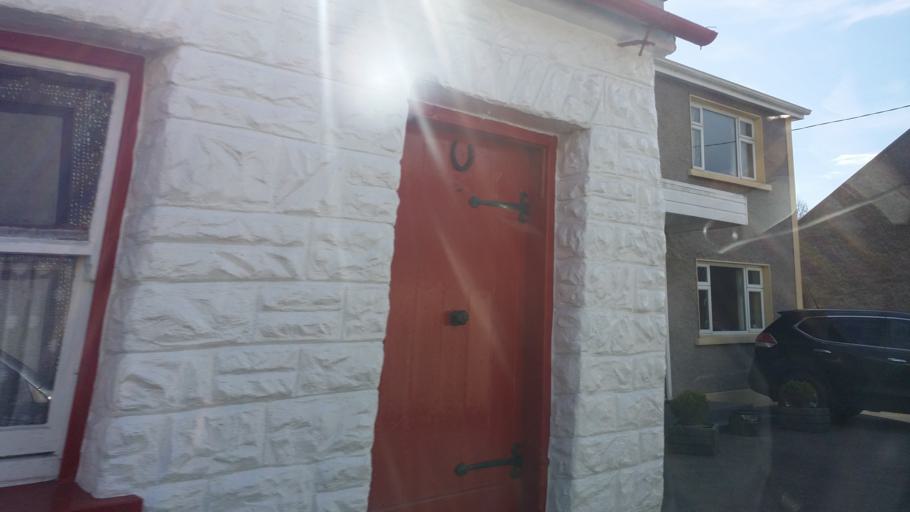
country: IE
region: Ulster
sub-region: County Donegal
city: Ballyshannon
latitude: 54.5037
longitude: -8.1927
